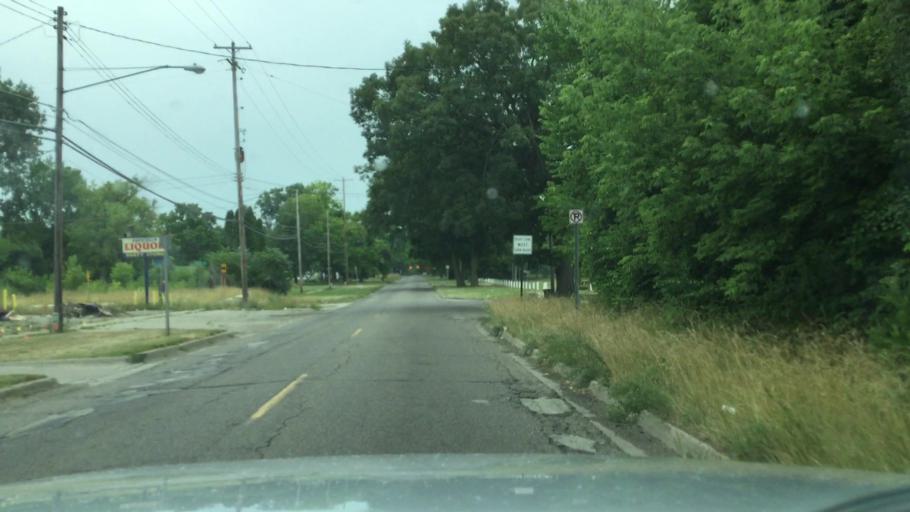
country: US
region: Michigan
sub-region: Genesee County
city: Beecher
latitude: 43.0584
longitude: -83.7236
